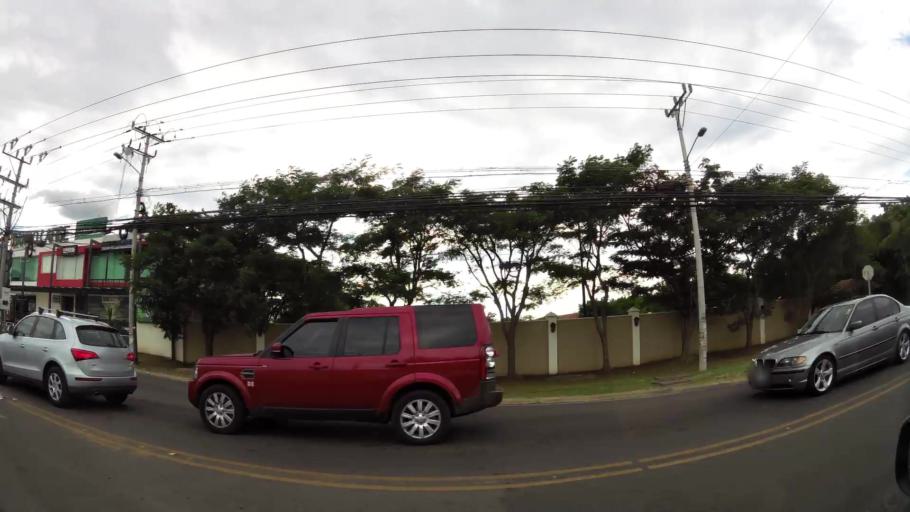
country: CR
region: San Jose
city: Santa Ana
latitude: 9.9543
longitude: -84.1947
